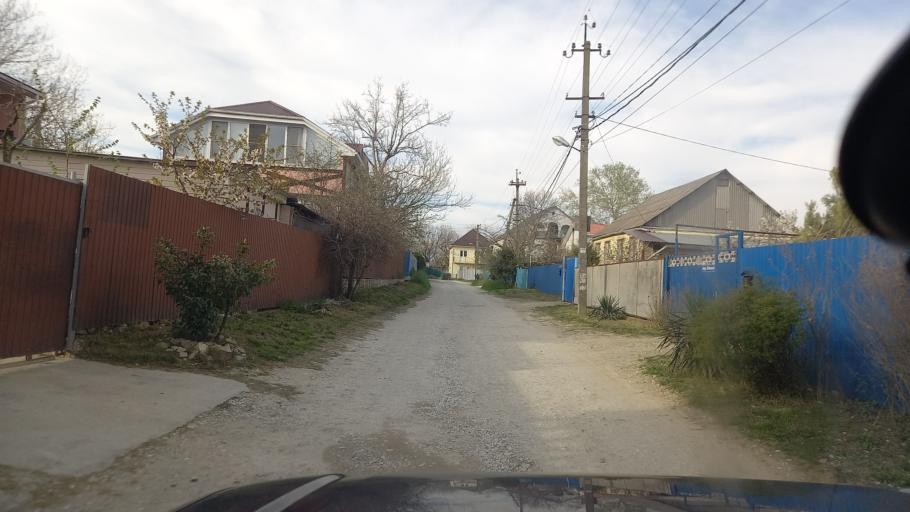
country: RU
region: Krasnodarskiy
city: Arkhipo-Osipovka
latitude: 44.3673
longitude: 38.5435
